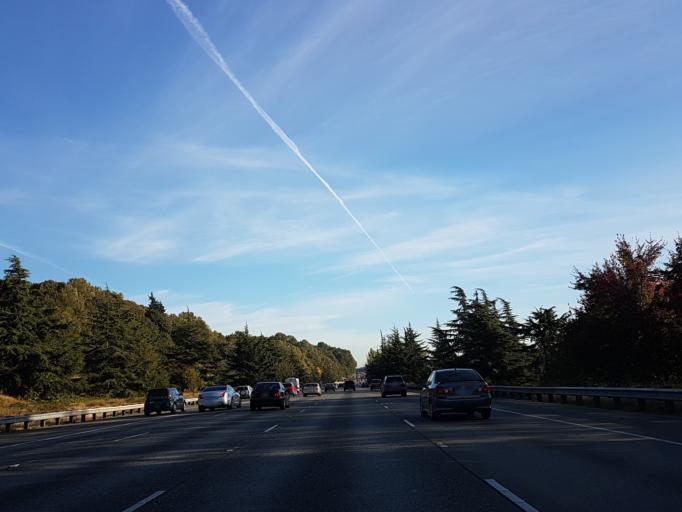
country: US
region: Washington
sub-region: King County
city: Boulevard Park
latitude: 47.5318
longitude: -122.2953
